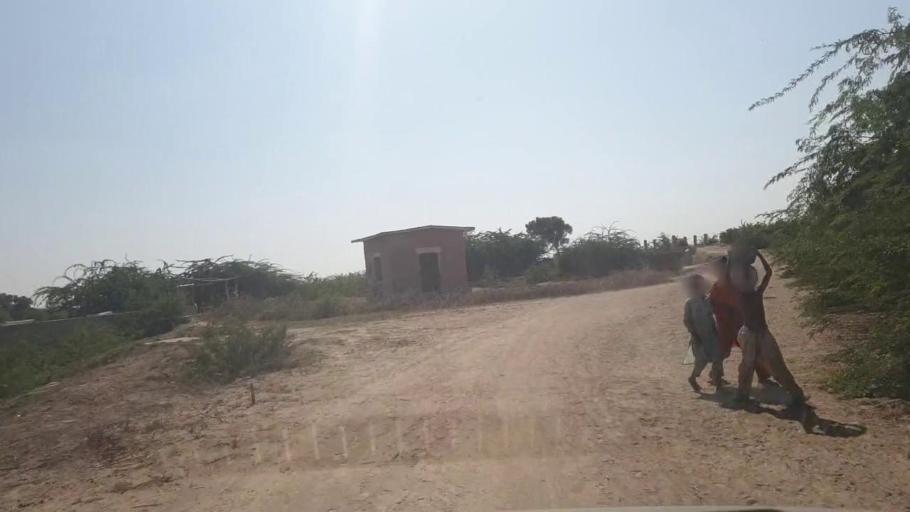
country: PK
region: Sindh
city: Tando Bago
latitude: 24.7661
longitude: 69.1542
